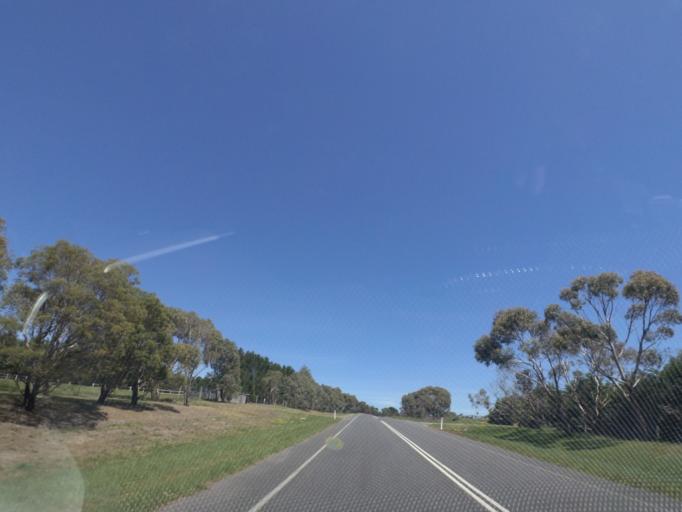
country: AU
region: Victoria
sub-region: Hume
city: Sunbury
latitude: -37.5421
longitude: 144.6354
